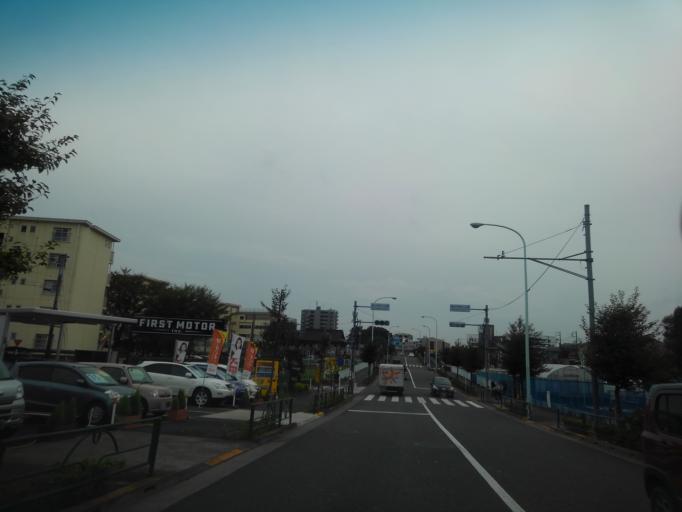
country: JP
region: Tokyo
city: Higashimurayama-shi
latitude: 35.7502
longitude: 139.4158
